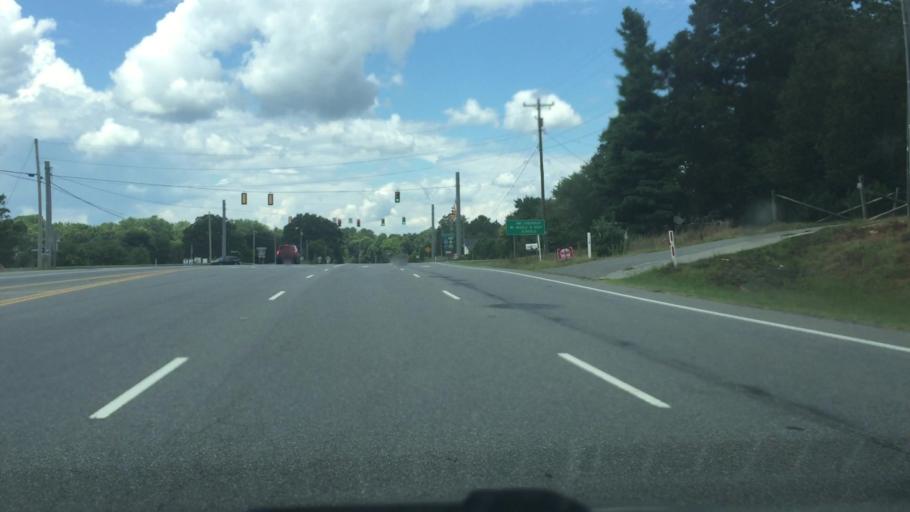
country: US
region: North Carolina
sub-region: Rowan County
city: Enochville
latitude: 35.4897
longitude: -80.6702
